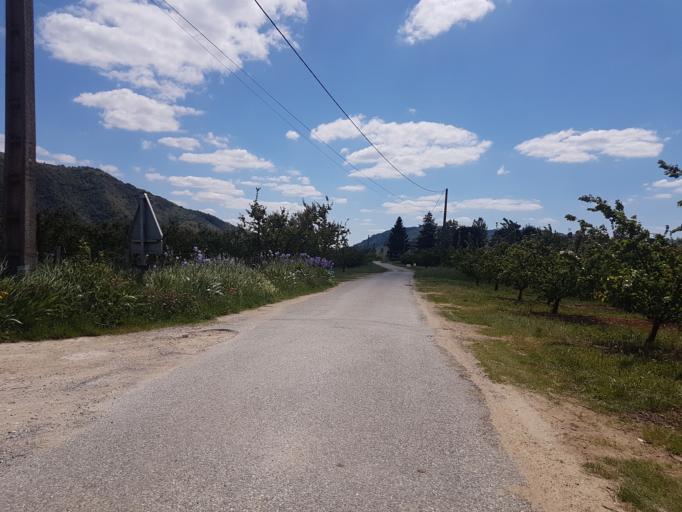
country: FR
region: Rhone-Alpes
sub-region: Departement de l'Ardeche
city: Saint-Jean-de-Muzols
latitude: 45.0957
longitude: 4.8230
